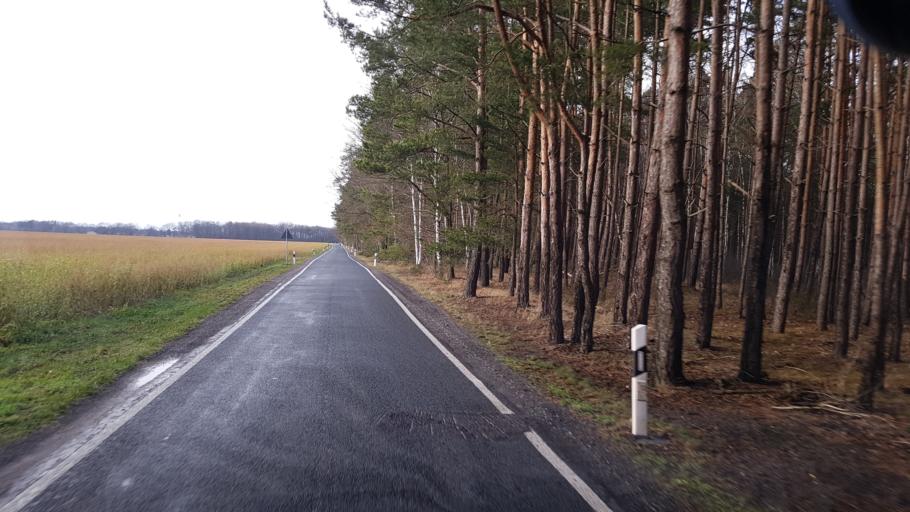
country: DE
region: Brandenburg
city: Bronkow
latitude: 51.6671
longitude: 13.9339
